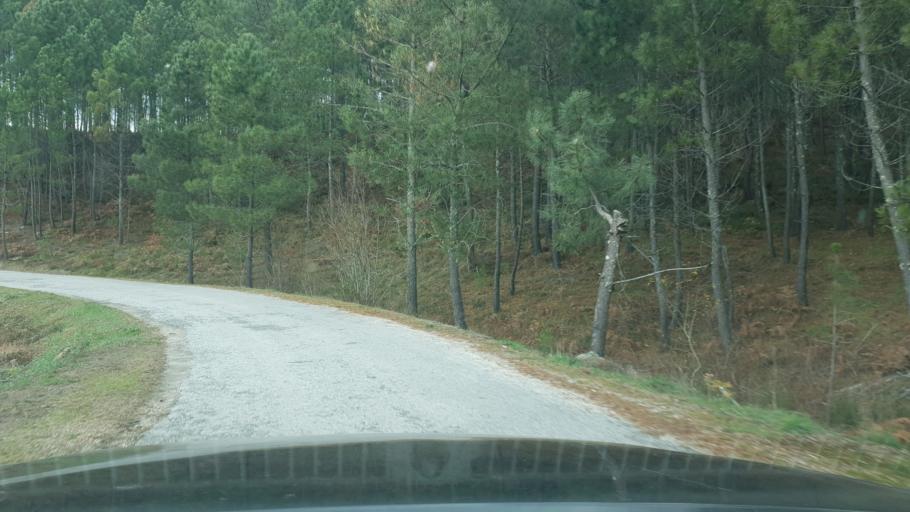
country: PT
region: Viseu
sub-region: Castro Daire
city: Castro Daire
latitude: 40.8813
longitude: -8.0076
